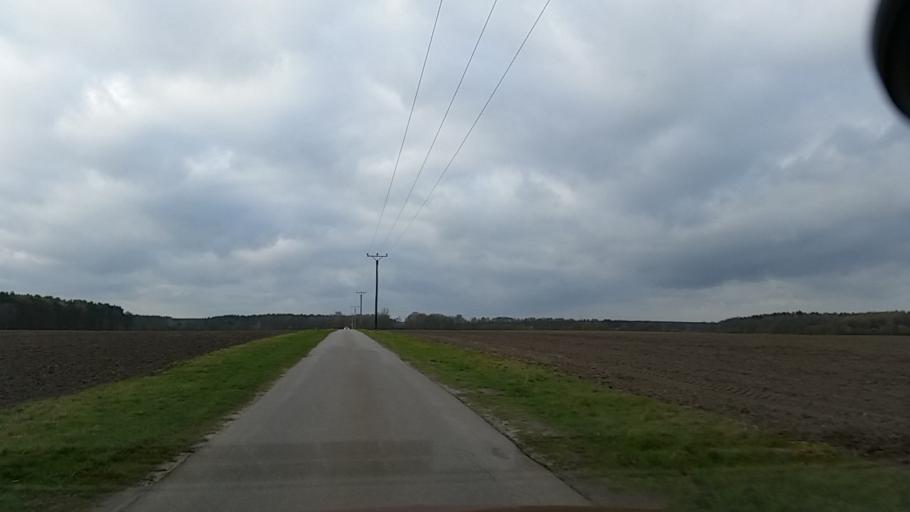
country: DE
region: Lower Saxony
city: Luder
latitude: 52.7653
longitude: 10.6813
